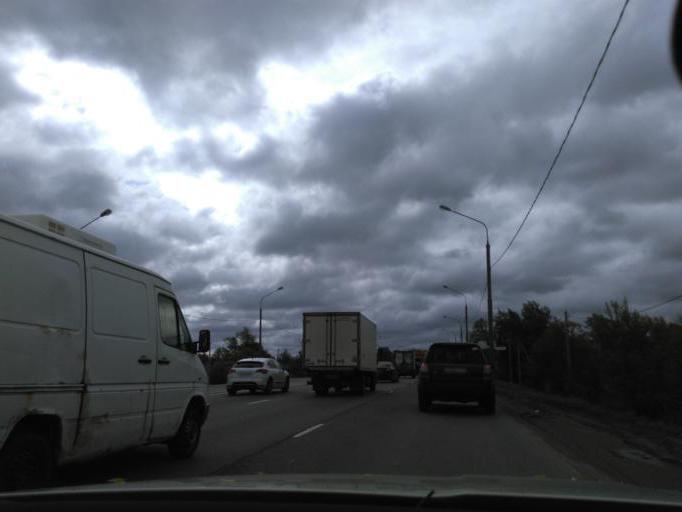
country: RU
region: Moskovskaya
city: Novopodrezkovo
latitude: 55.9373
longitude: 37.3692
